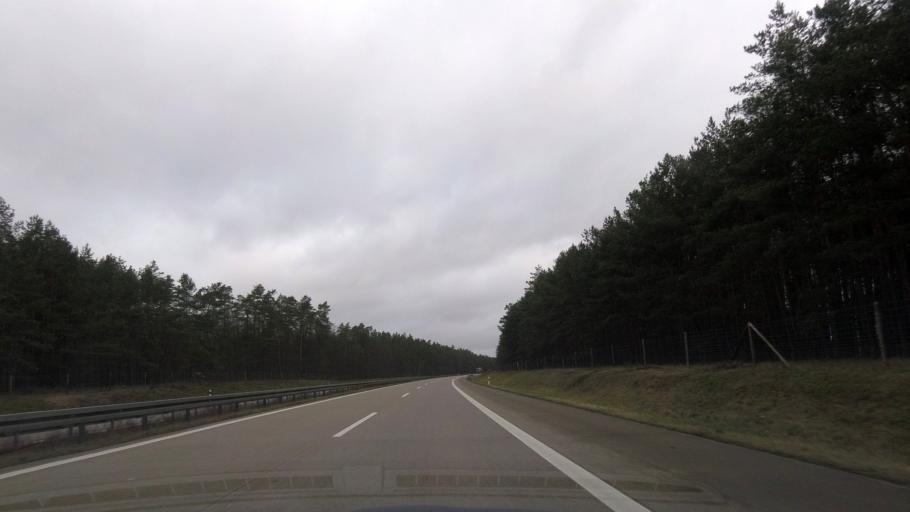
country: DE
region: Mecklenburg-Vorpommern
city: Krakow am See
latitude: 53.5670
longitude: 12.3166
